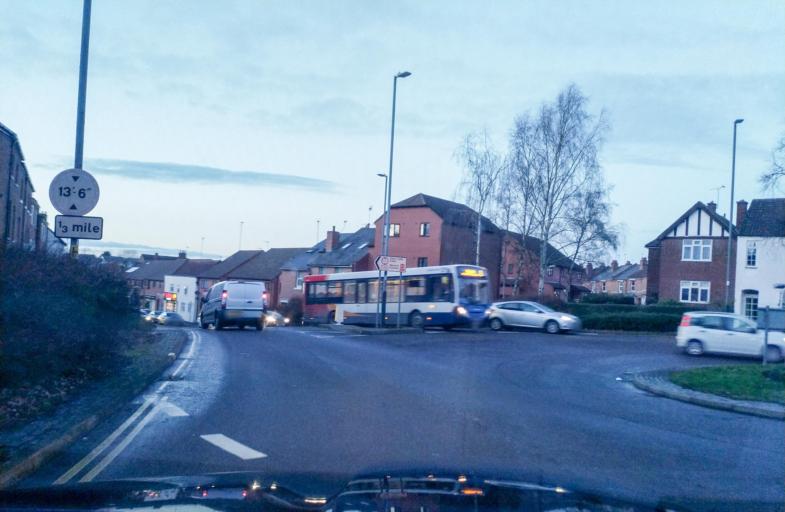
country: GB
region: England
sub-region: Warwickshire
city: Warwick
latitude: 52.2837
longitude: -1.5912
